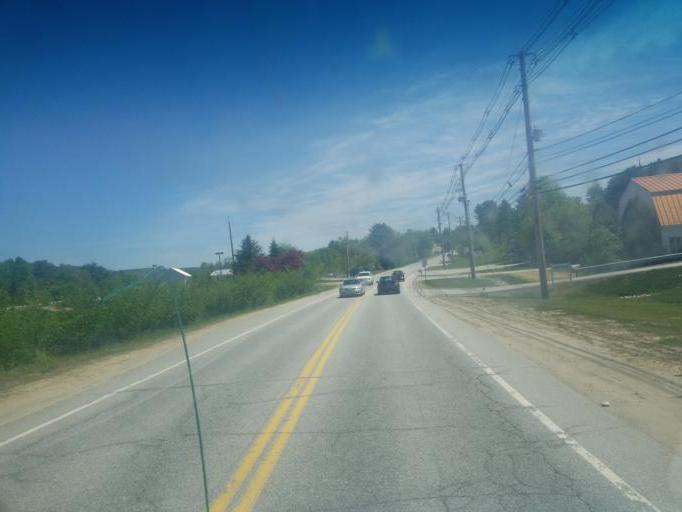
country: US
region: New Hampshire
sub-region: Grafton County
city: Plymouth
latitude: 43.7702
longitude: -71.7212
